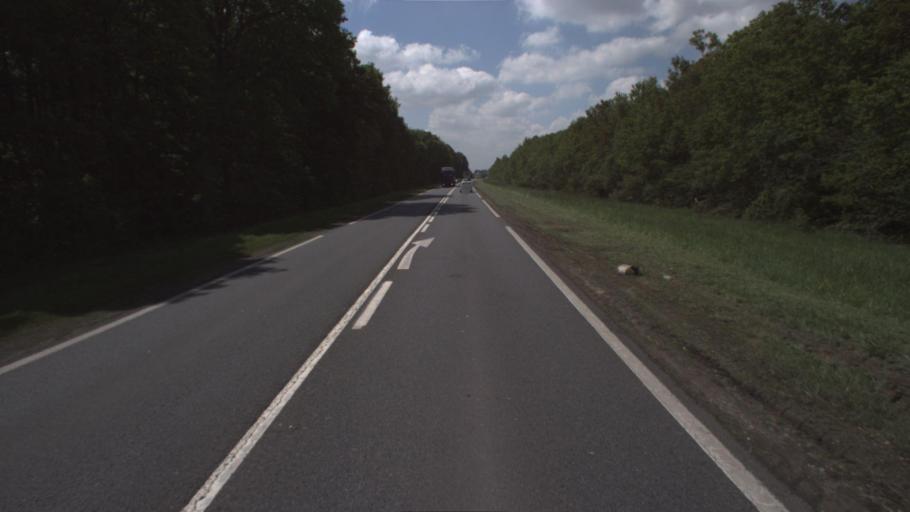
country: FR
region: Ile-de-France
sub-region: Departement de Seine-et-Marne
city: Guignes
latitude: 48.6492
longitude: 2.8021
